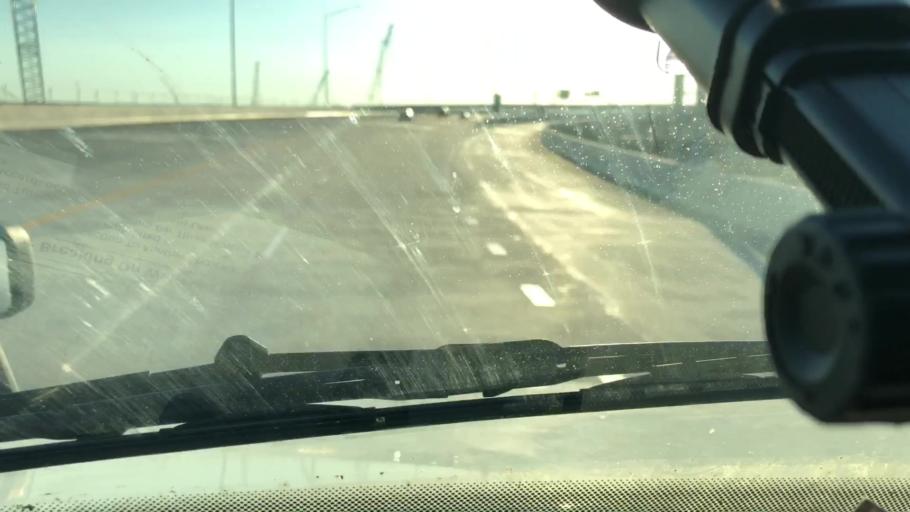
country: US
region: Iowa
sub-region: Pottawattamie County
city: Council Bluffs
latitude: 41.2322
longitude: -95.8323
